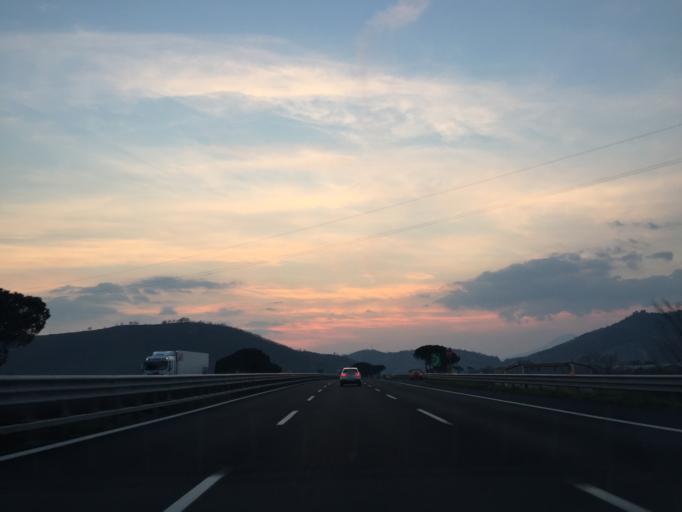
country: IT
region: Campania
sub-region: Provincia di Salerno
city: Roccapiemonte
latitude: 40.7670
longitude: 14.6874
